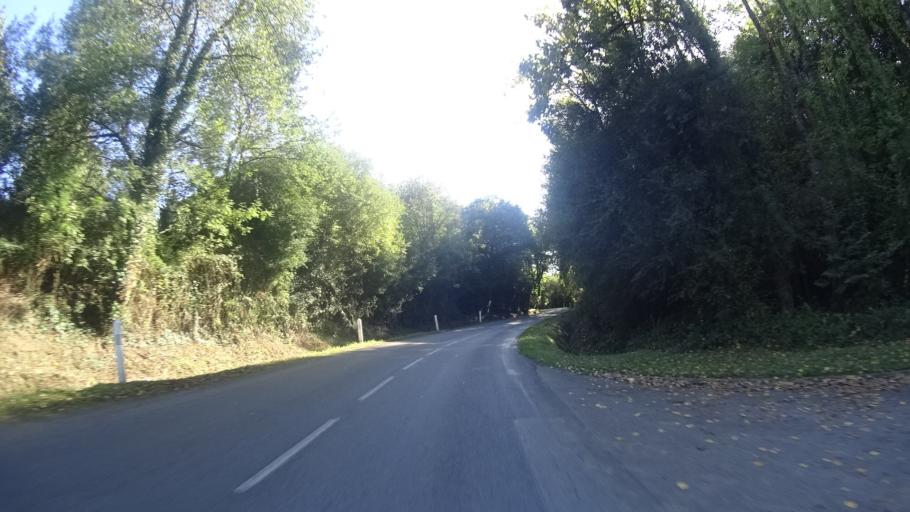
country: FR
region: Brittany
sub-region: Departement du Morbihan
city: Peillac
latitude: 47.7201
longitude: -2.2139
